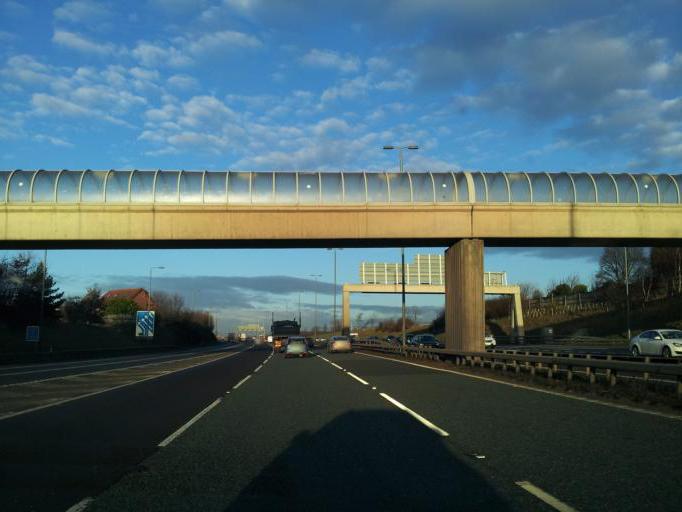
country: GB
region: England
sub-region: City and Borough of Leeds
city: Lofthouse
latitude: 53.7335
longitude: -1.5248
